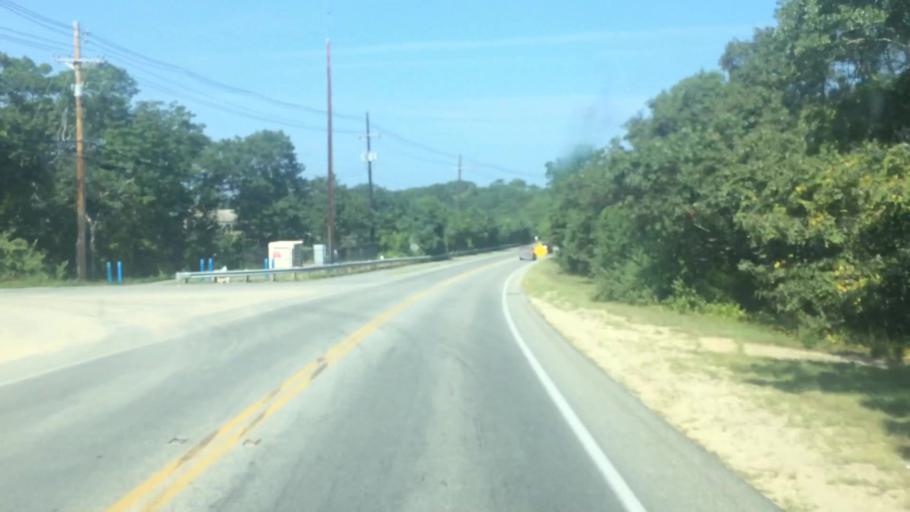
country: US
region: Massachusetts
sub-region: Dukes County
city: Vineyard Haven
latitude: 41.4215
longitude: -70.6035
